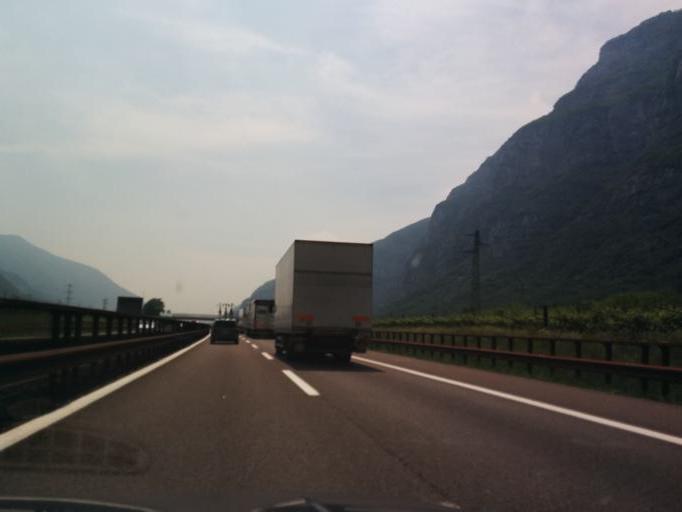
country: IT
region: Veneto
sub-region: Provincia di Verona
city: Rivalta
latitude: 45.6365
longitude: 10.8743
